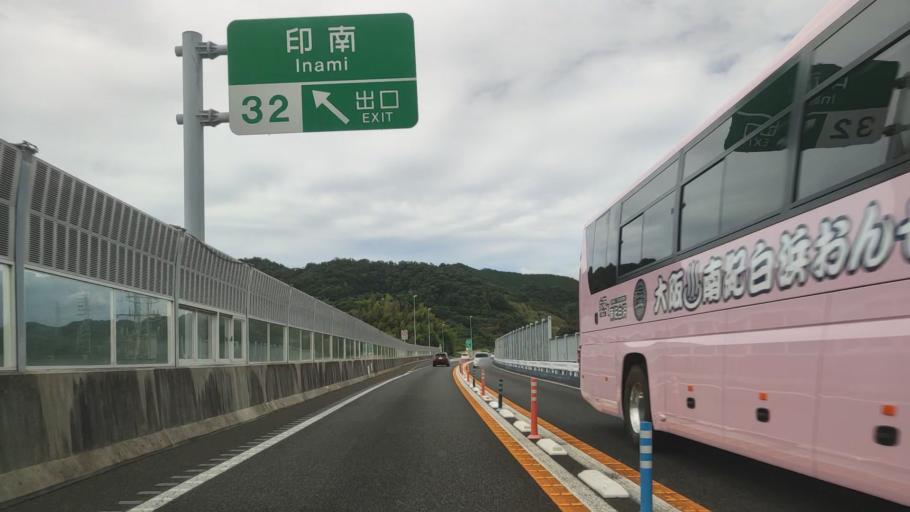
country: JP
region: Wakayama
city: Gobo
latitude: 33.8229
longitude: 135.2215
